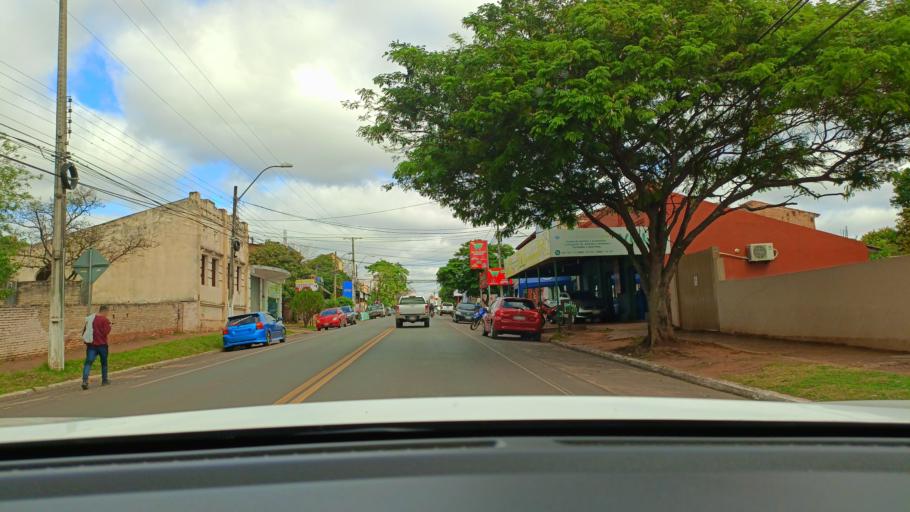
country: PY
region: San Pedro
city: Guayaybi
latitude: -24.6676
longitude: -56.4448
